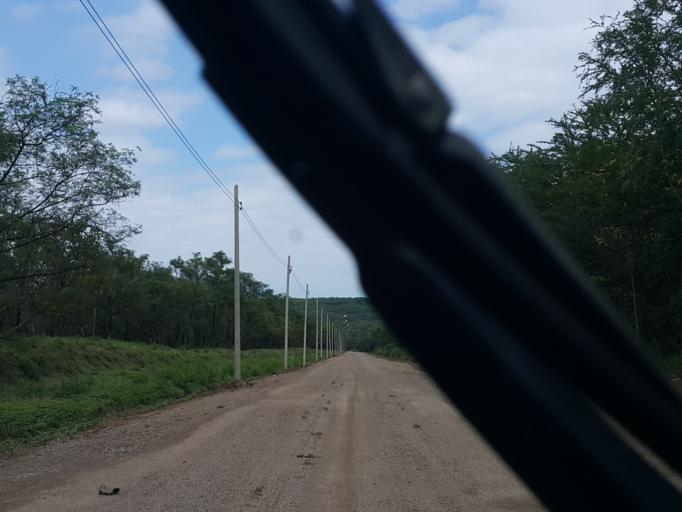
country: TH
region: Lampang
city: Mae Mo
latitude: 18.3171
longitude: 99.7476
